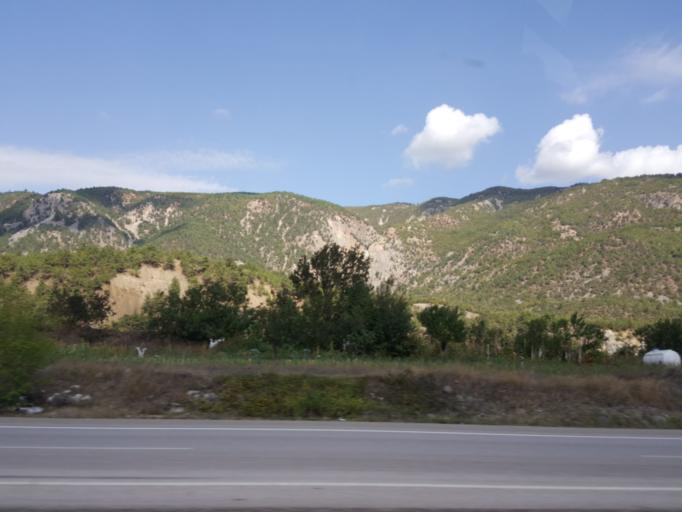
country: TR
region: Tokat
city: Basciftlik
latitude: 40.4167
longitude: 37.1909
